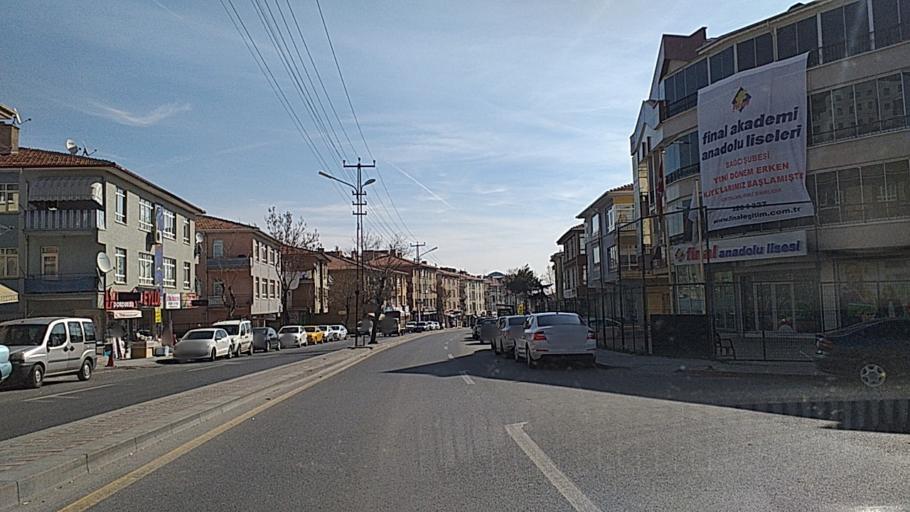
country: TR
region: Ankara
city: Ankara
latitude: 39.9846
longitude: 32.8293
